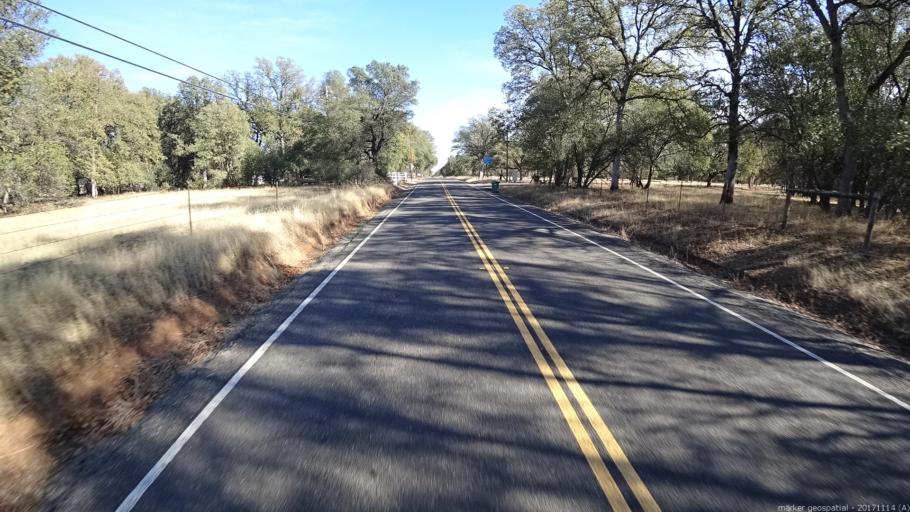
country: US
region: California
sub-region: Shasta County
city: Anderson
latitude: 40.3883
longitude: -122.4452
